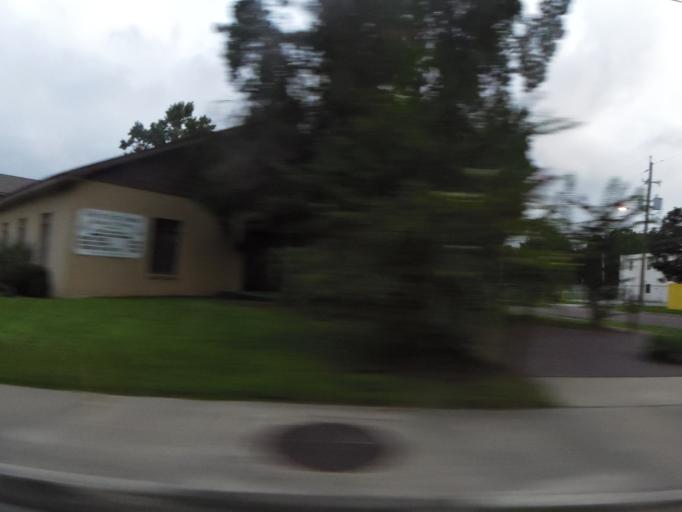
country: US
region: Florida
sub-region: Duval County
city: Jacksonville
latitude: 30.3219
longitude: -81.7117
